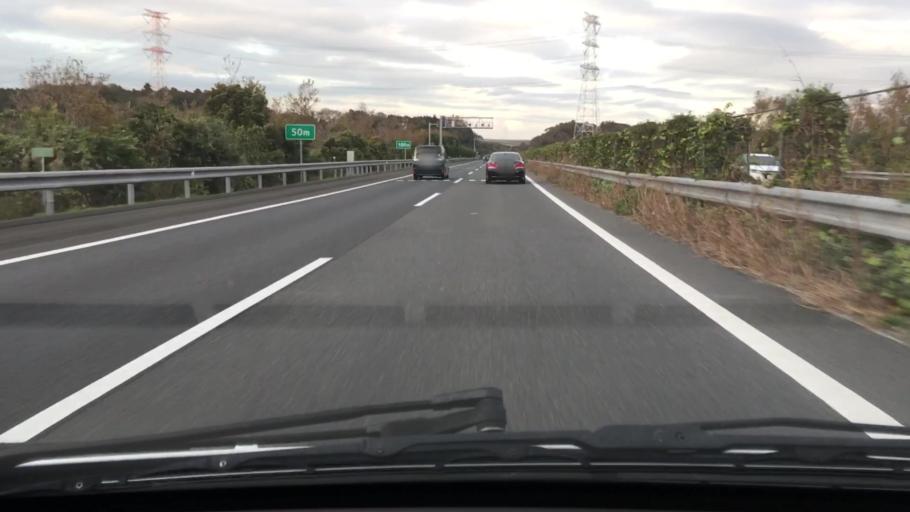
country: JP
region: Chiba
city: Kisarazu
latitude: 35.4107
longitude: 140.0097
